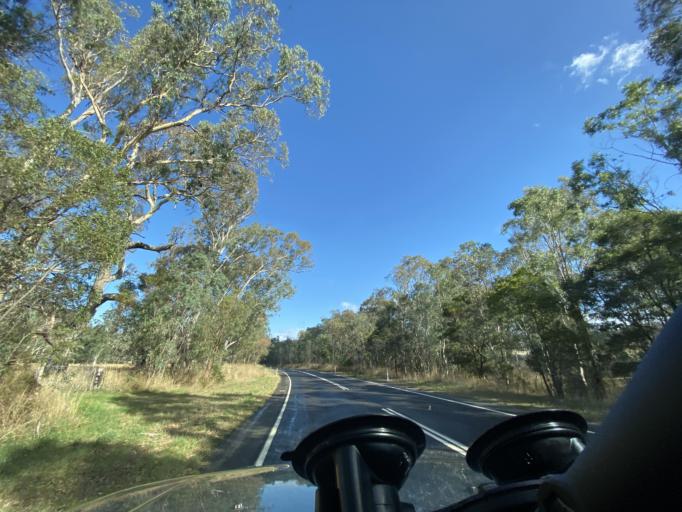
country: AU
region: Victoria
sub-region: Murrindindi
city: Kinglake West
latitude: -37.2710
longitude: 145.3617
